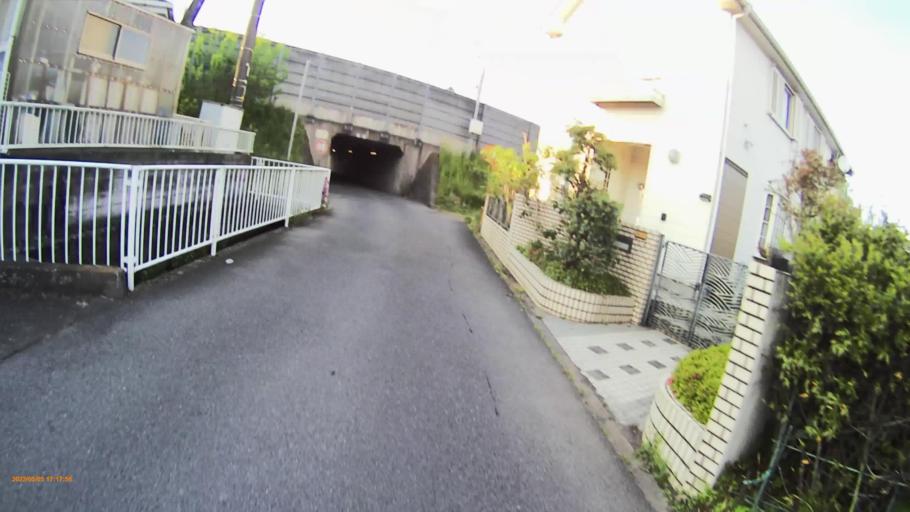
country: JP
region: Saitama
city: Kurihashi
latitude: 36.1323
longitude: 139.7070
